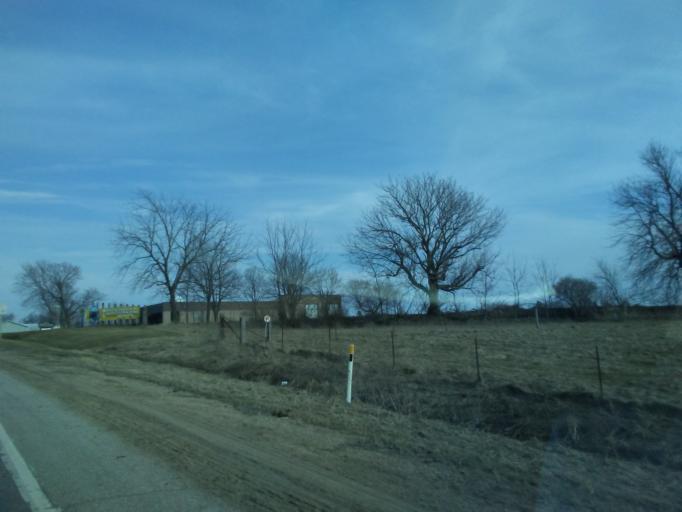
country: US
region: Wisconsin
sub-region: Grant County
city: Fennimore
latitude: 42.9884
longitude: -90.6636
